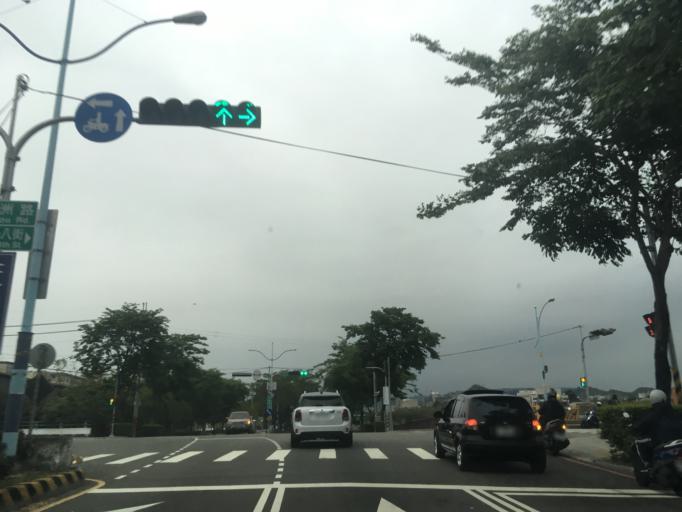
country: TW
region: Taiwan
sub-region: Taichung City
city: Taichung
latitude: 24.1423
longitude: 120.7213
